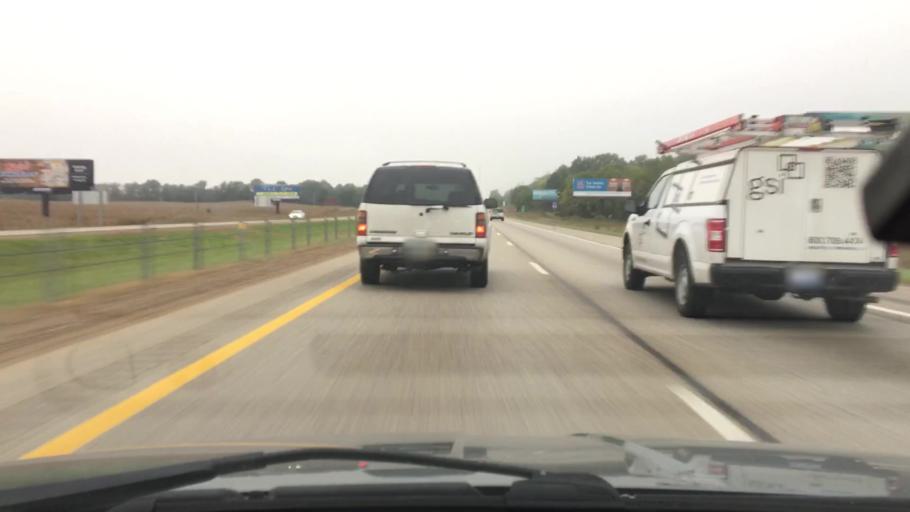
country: US
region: Michigan
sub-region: Calhoun County
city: Springfield
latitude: 42.2740
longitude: -85.3026
